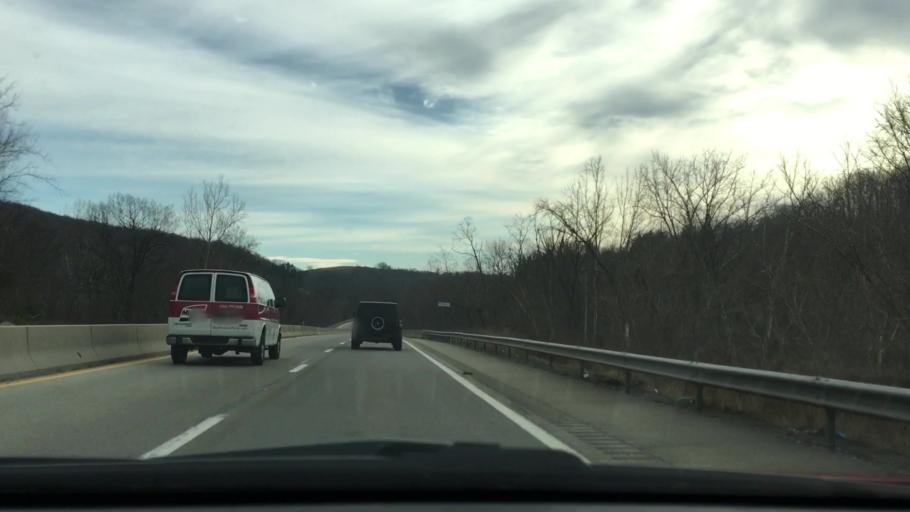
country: US
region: Pennsylvania
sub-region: Fayette County
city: Oliver
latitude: 39.9753
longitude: -79.7599
